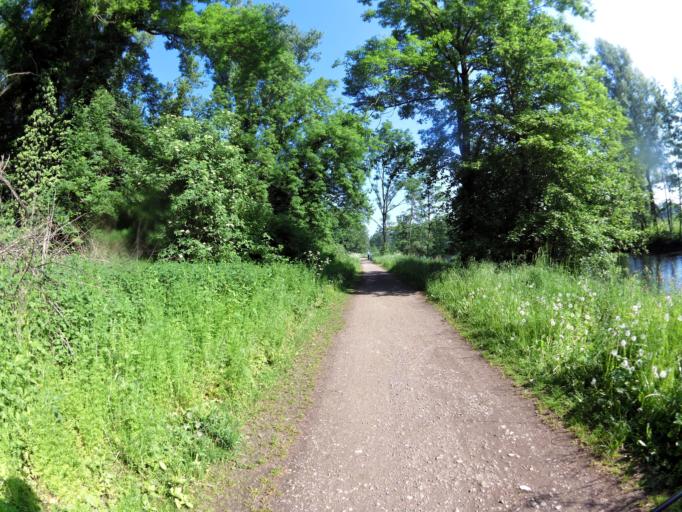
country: DE
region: North Rhine-Westphalia
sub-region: Regierungsbezirk Koln
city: Linnich
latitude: 50.9581
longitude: 6.2901
